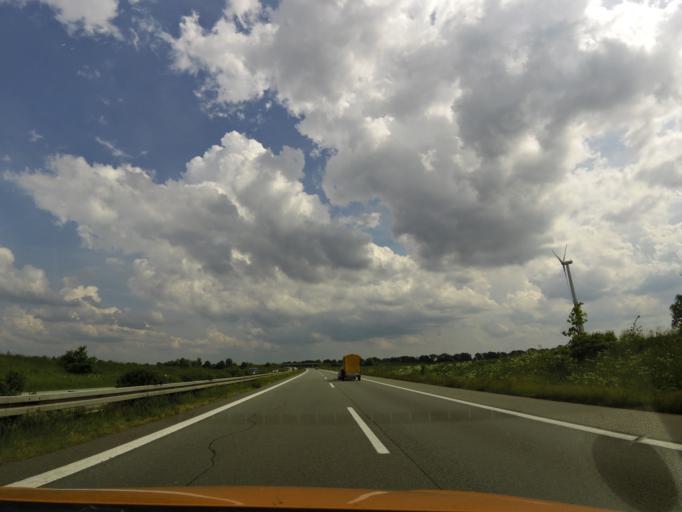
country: DE
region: Brandenburg
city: Heiligengrabe
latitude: 53.1829
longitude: 12.2949
